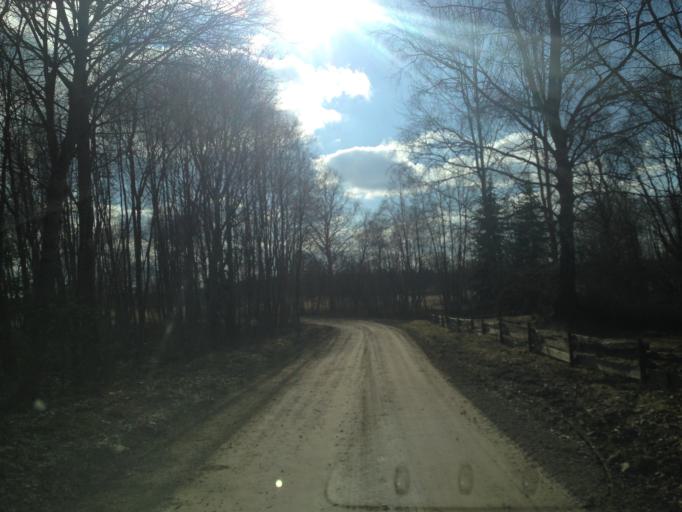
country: EE
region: Harju
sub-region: Nissi vald
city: Riisipere
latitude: 59.1379
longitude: 24.4346
